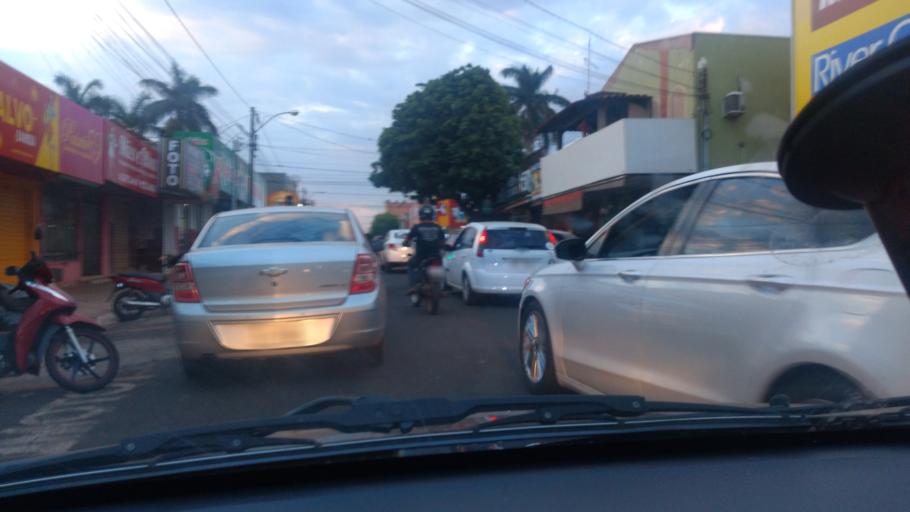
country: BR
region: Goias
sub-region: Santa Helena De Goias
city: Santa Helena de Goias
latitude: -17.7951
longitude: -50.9307
